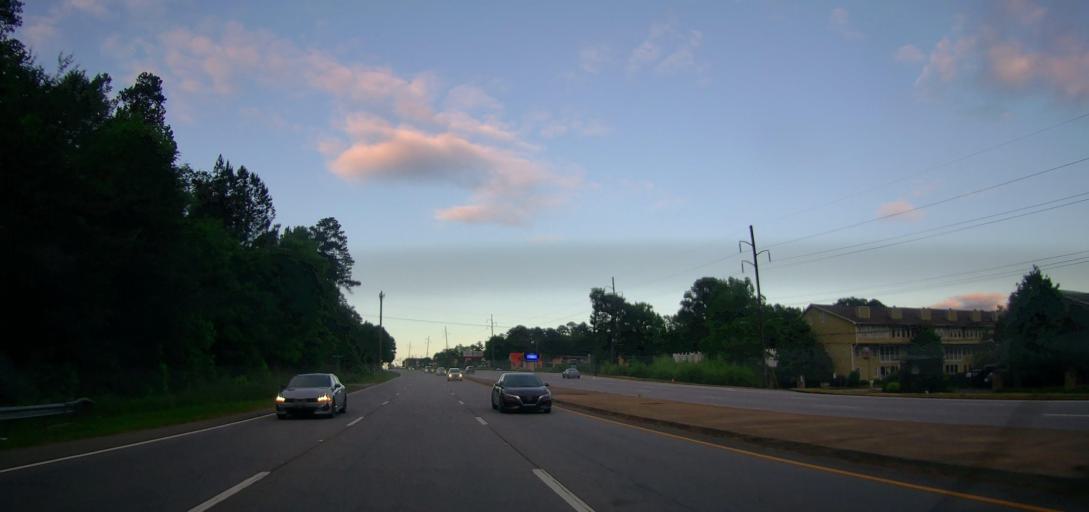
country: US
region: Georgia
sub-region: Clarke County
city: Country Club Estates
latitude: 33.9471
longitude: -83.4223
